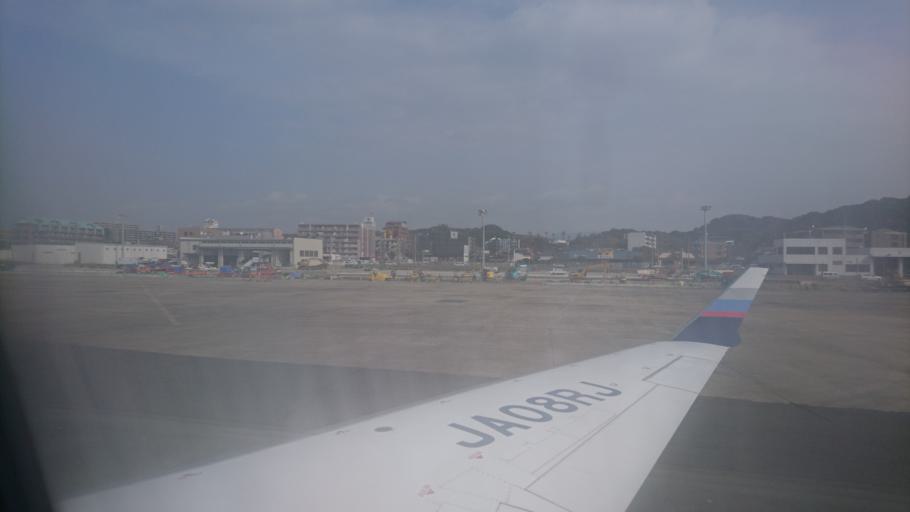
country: JP
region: Fukuoka
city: Fukuoka-shi
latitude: 33.5858
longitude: 130.4531
